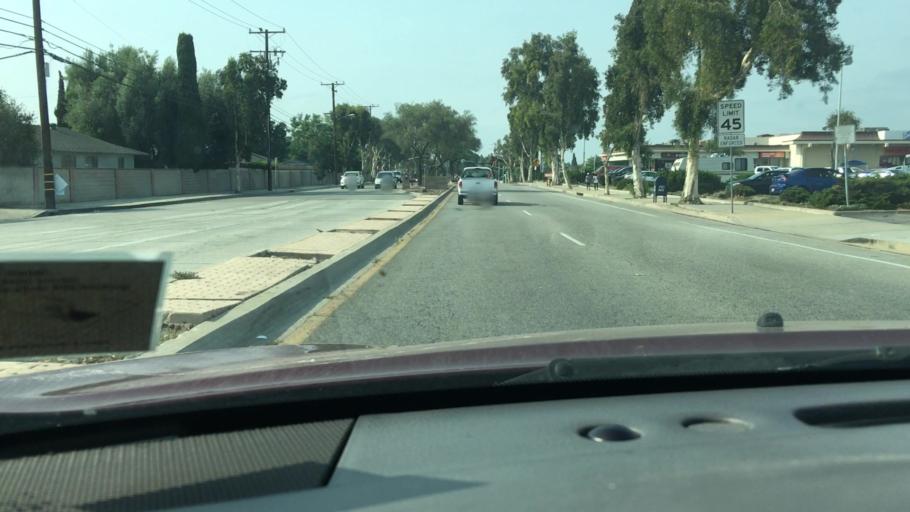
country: US
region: California
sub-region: Los Angeles County
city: La Mirada
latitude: 33.9166
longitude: -118.0293
